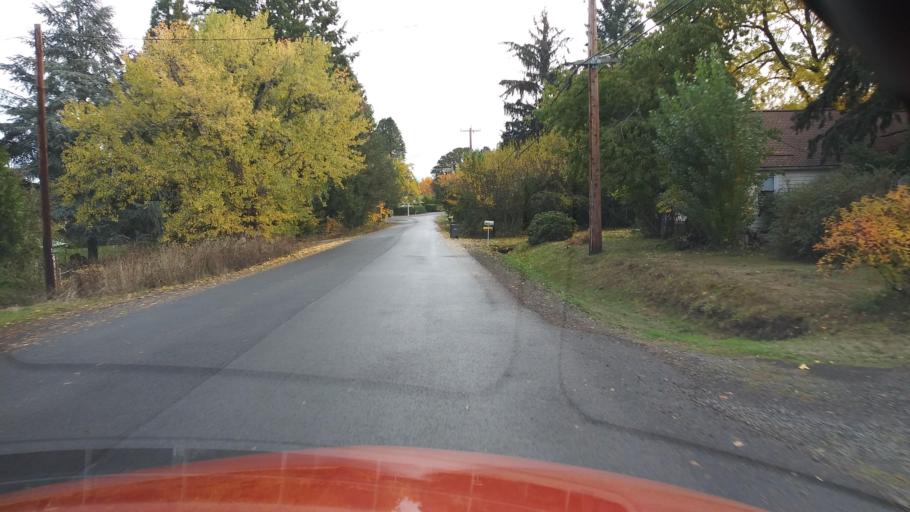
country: US
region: Oregon
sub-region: Washington County
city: Forest Grove
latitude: 45.5323
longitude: -123.1303
